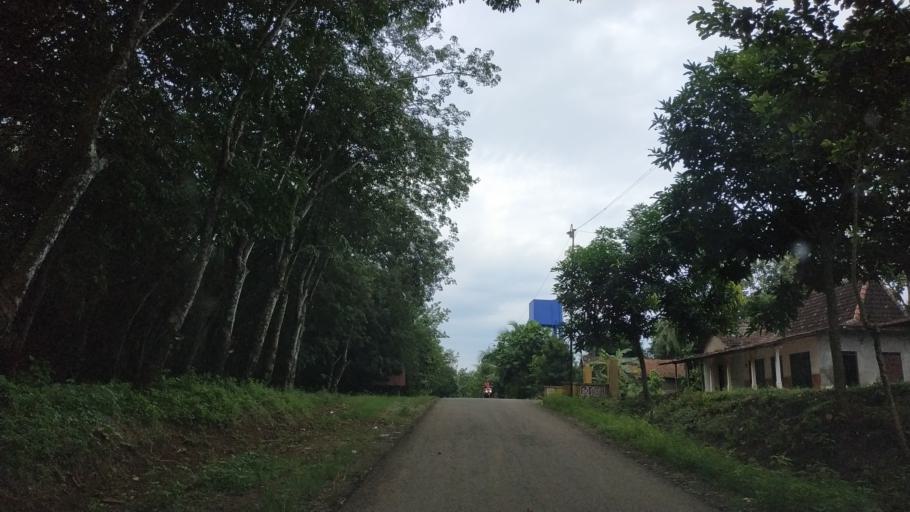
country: ID
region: Central Java
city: Krajan Tegalombo
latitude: -6.4312
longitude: 110.9833
